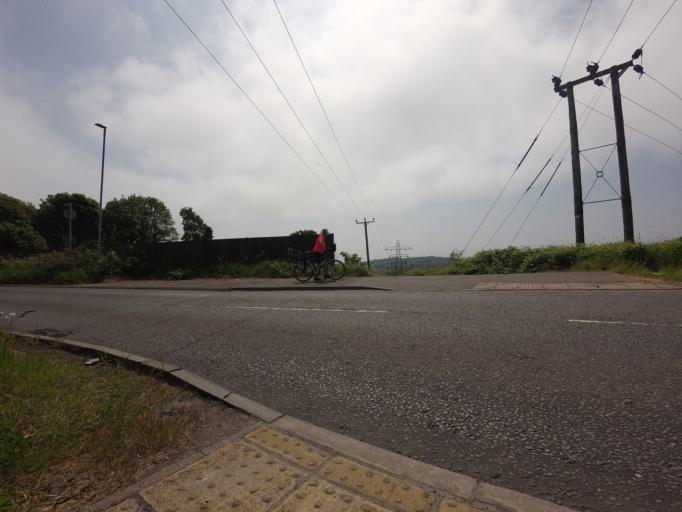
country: GB
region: Scotland
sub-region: Fife
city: Inverkeithing
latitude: 56.0465
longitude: -3.4069
